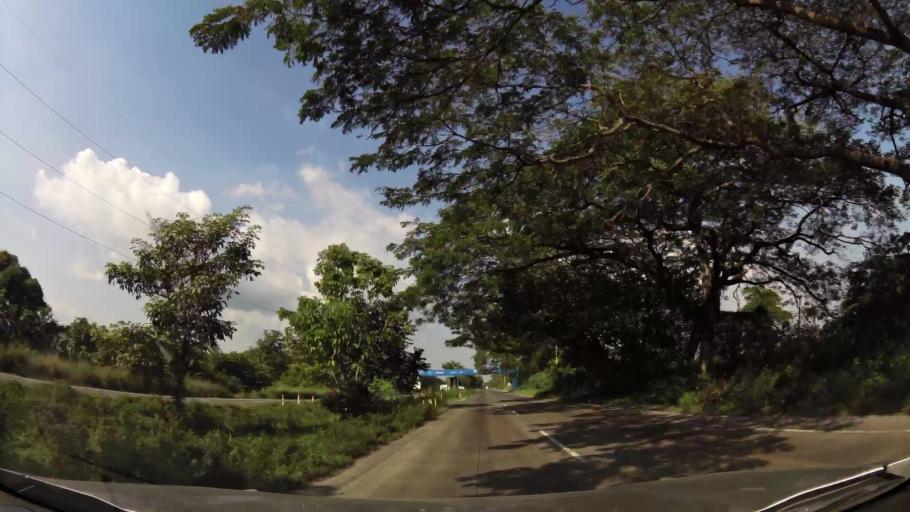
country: GT
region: Escuintla
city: Puerto San Jose
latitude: 14.0072
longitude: -90.7859
